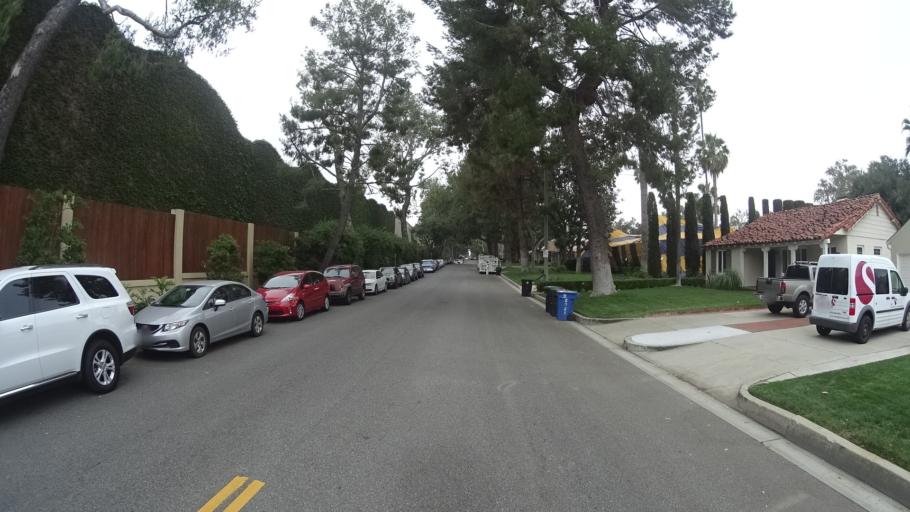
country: US
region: California
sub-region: Los Angeles County
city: Burbank
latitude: 34.1565
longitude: -118.3225
